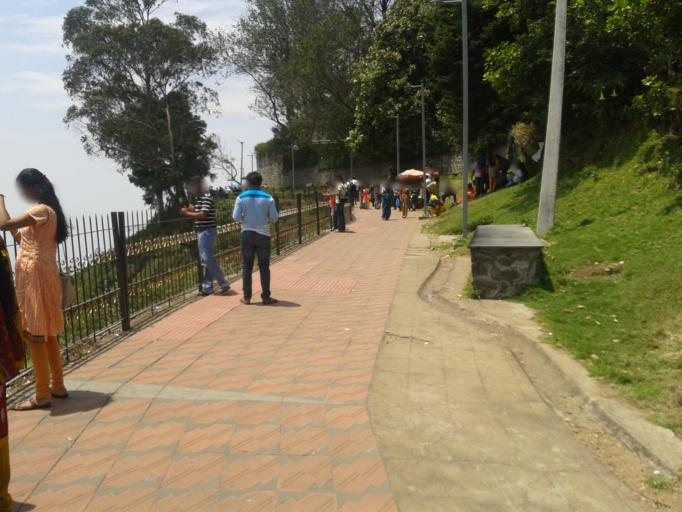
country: IN
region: Tamil Nadu
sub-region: Dindigul
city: Kodaikanal
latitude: 10.2319
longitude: 77.4944
